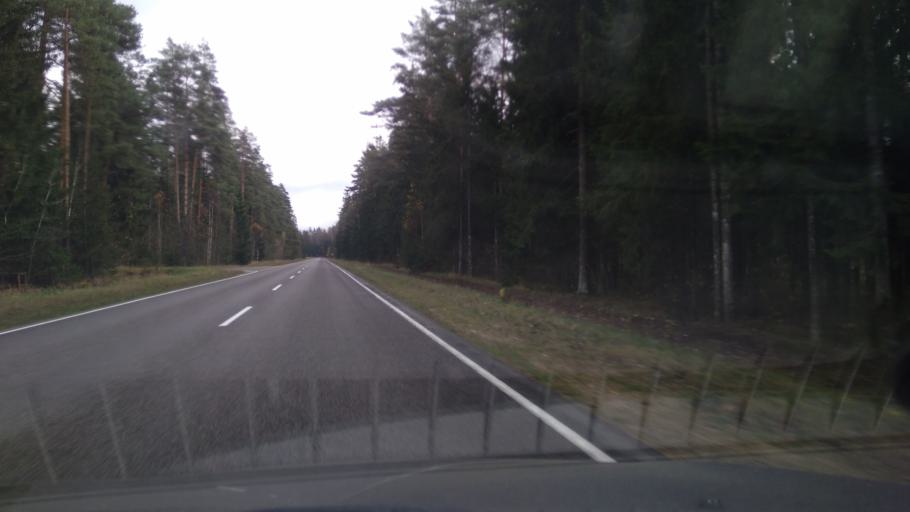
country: BY
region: Minsk
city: Urechcha
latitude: 53.2061
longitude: 27.7919
